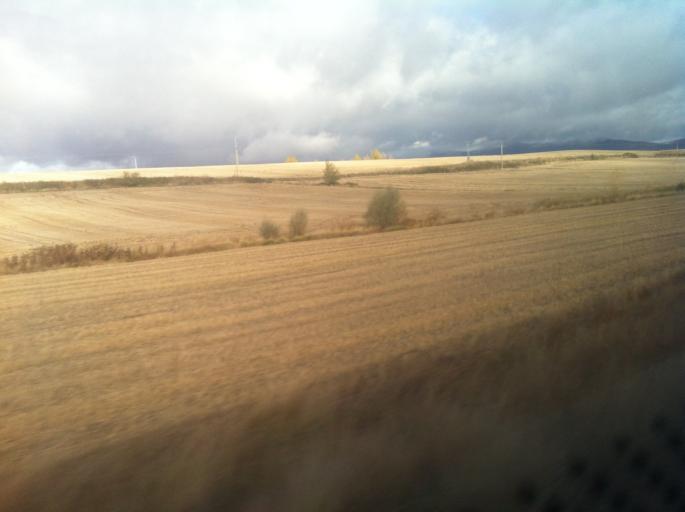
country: ES
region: Castille and Leon
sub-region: Provincia de Burgos
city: Grisalena
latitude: 42.6007
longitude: -3.2870
